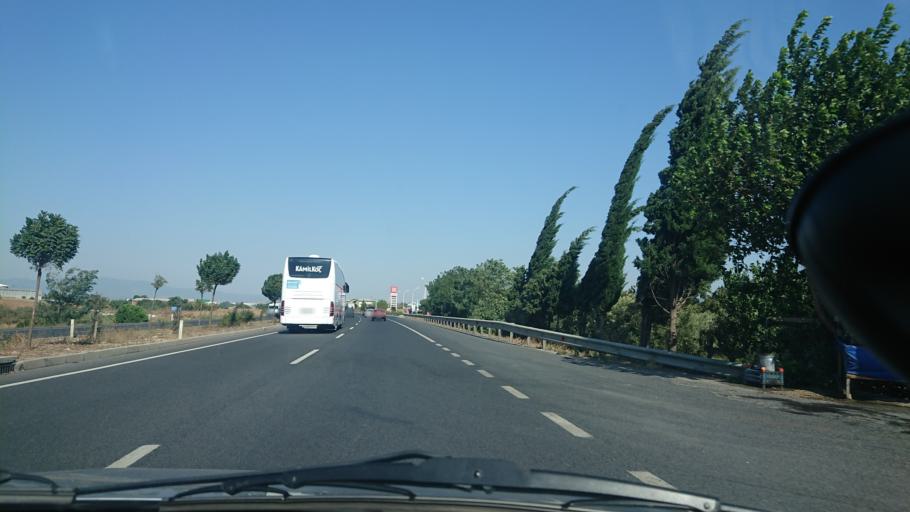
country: TR
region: Manisa
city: Karaoglanli
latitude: 38.4535
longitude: 27.5713
